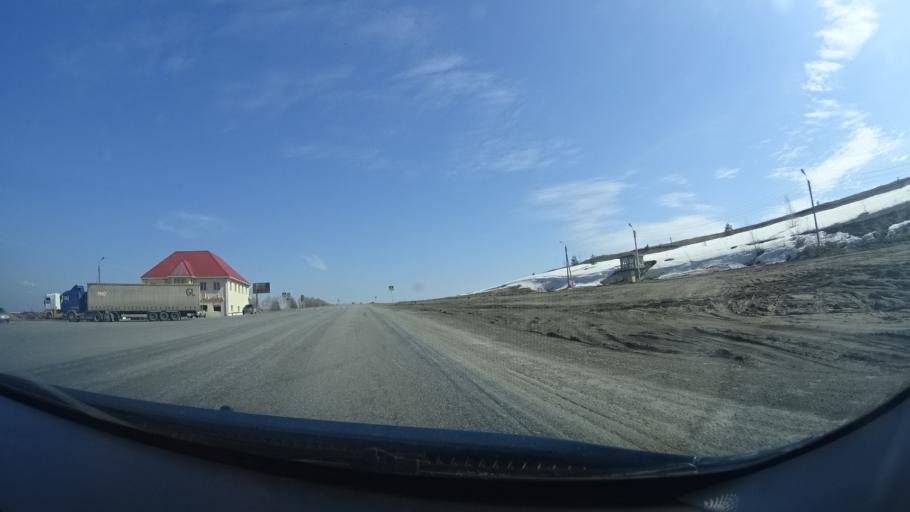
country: RU
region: Bashkortostan
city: Nizhnetroitskiy
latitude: 54.4560
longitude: 53.6820
